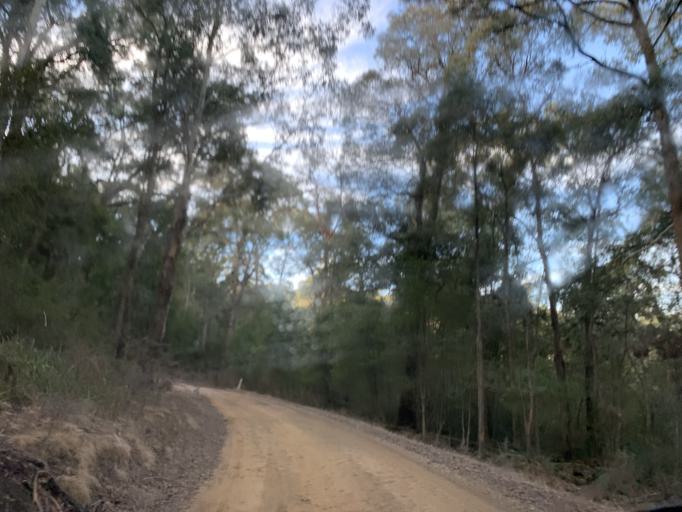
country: AU
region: Victoria
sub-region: Mansfield
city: Mansfield
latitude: -36.8900
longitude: 146.1203
